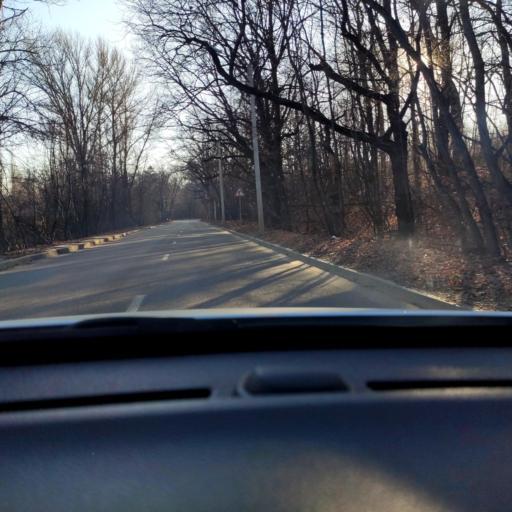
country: RU
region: Voronezj
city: Voronezh
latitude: 51.7240
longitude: 39.2356
